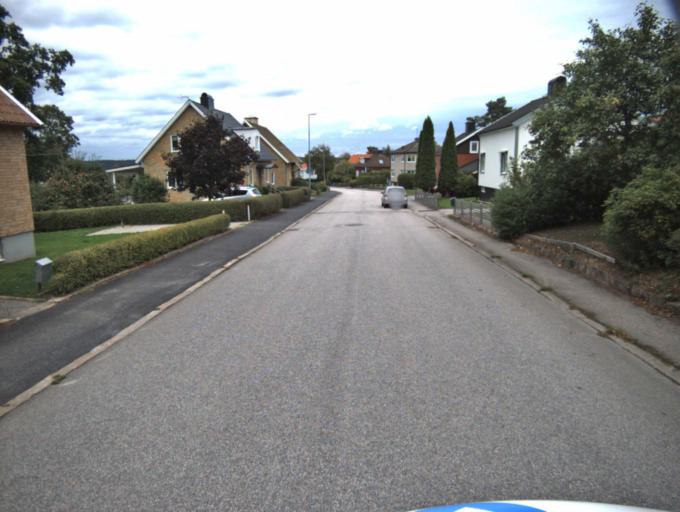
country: SE
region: Vaestra Goetaland
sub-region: Ulricehamns Kommun
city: Ulricehamn
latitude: 57.7842
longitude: 13.4179
